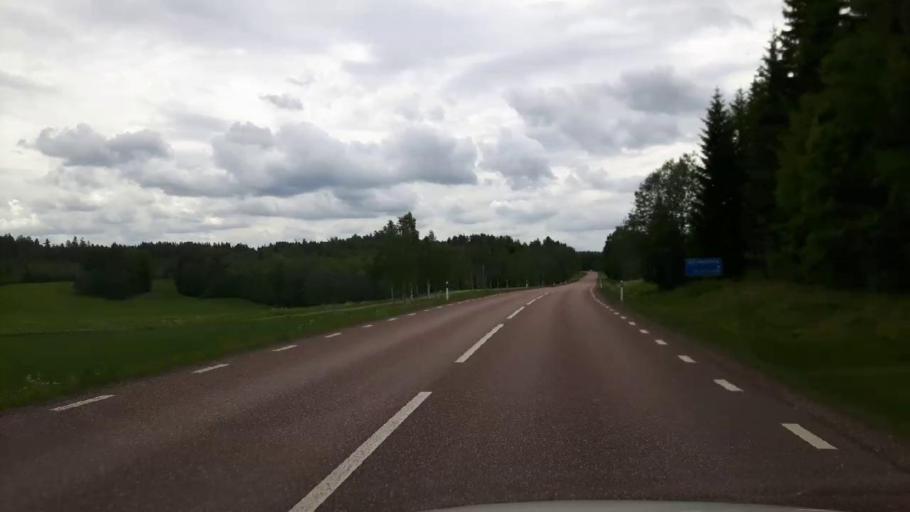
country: SE
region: Dalarna
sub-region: Hedemora Kommun
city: Brunna
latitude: 60.2147
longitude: 15.9918
